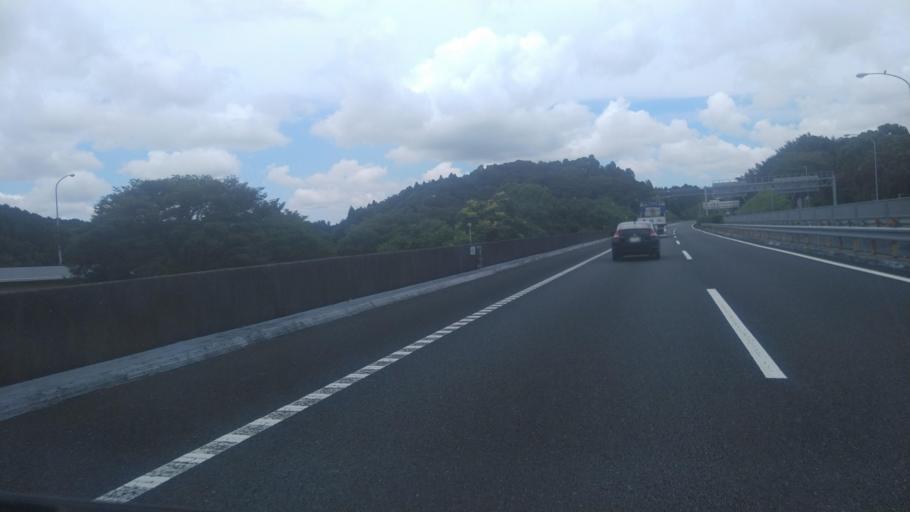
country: JP
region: Chiba
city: Narita
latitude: 35.7851
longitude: 140.3457
